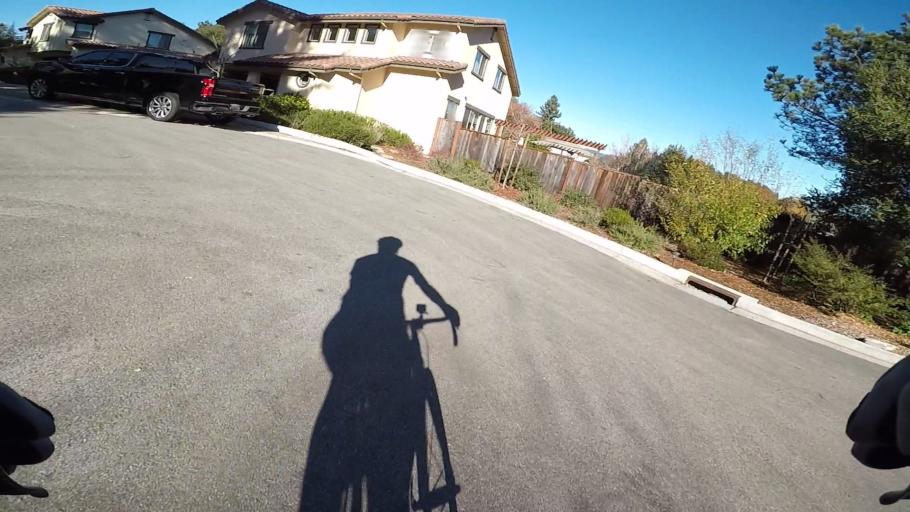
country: US
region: California
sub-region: Santa Cruz County
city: Scotts Valley
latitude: 37.0425
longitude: -122.0336
